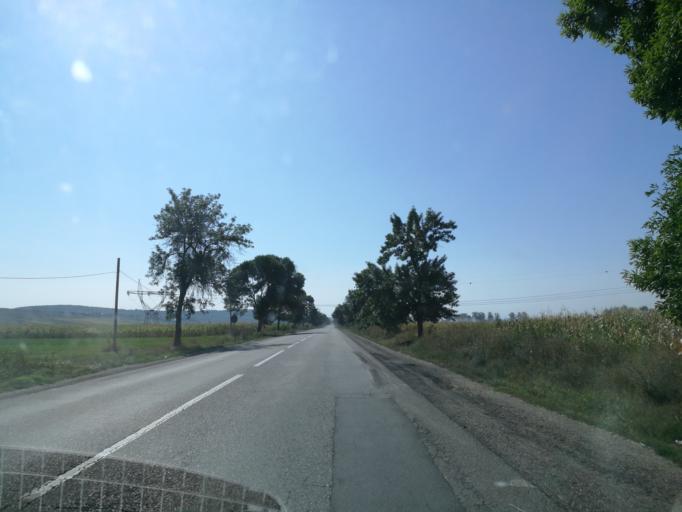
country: RO
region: Iasi
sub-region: Comuna Motca
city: Motca
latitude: 47.2265
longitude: 26.5988
